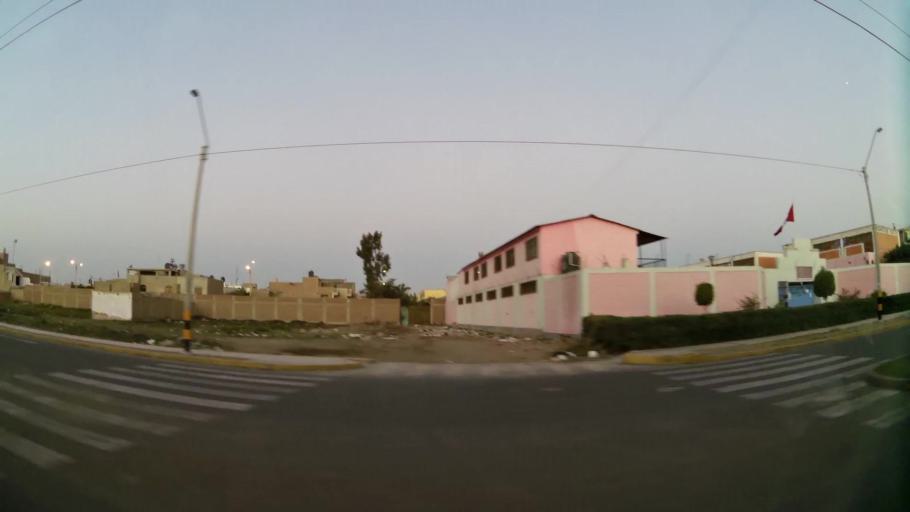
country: PE
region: Ica
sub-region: Provincia de Pisco
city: Pisco
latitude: -13.7081
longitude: -76.2084
